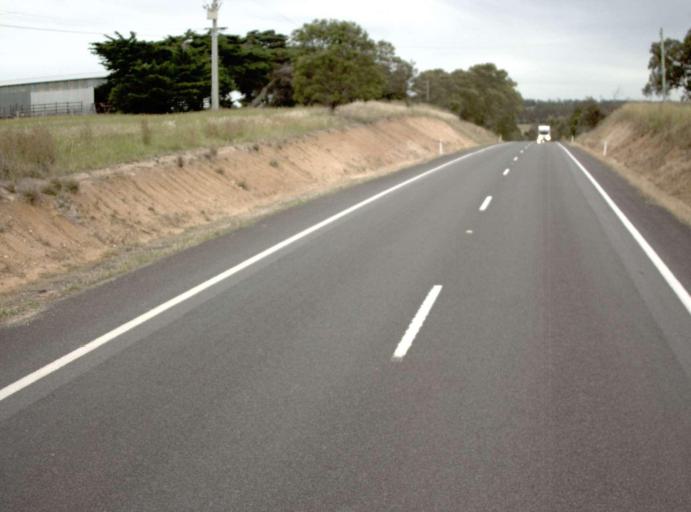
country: AU
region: Victoria
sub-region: Wellington
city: Sale
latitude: -38.2877
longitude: 147.0366
